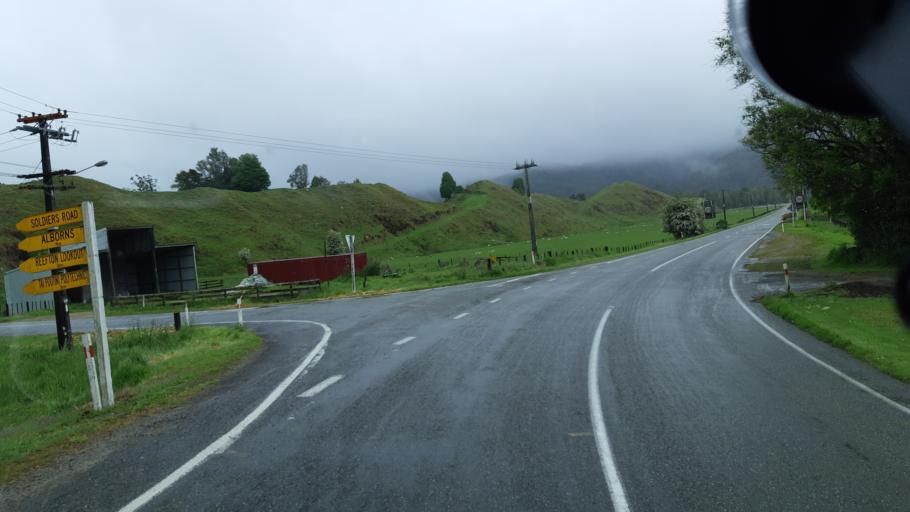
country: NZ
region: West Coast
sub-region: Buller District
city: Westport
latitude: -42.1227
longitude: 171.8546
